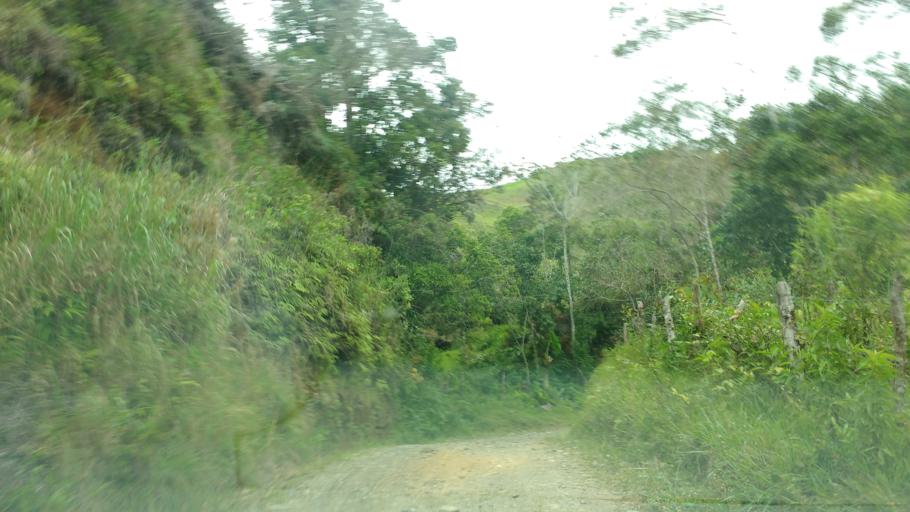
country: CO
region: Antioquia
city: Concepcion
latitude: 6.3690
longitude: -75.2295
